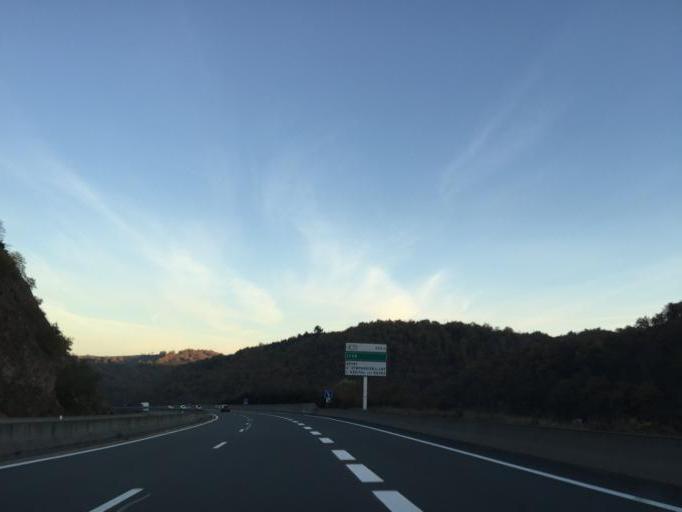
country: FR
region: Rhone-Alpes
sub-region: Departement de la Loire
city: Neulise
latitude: 45.9538
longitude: 4.1352
